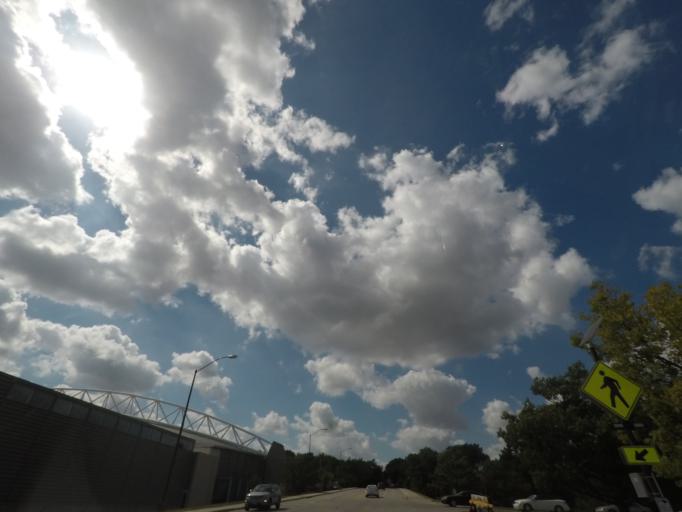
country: US
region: Iowa
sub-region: Story County
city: Ames
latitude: 42.0163
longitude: -93.6368
